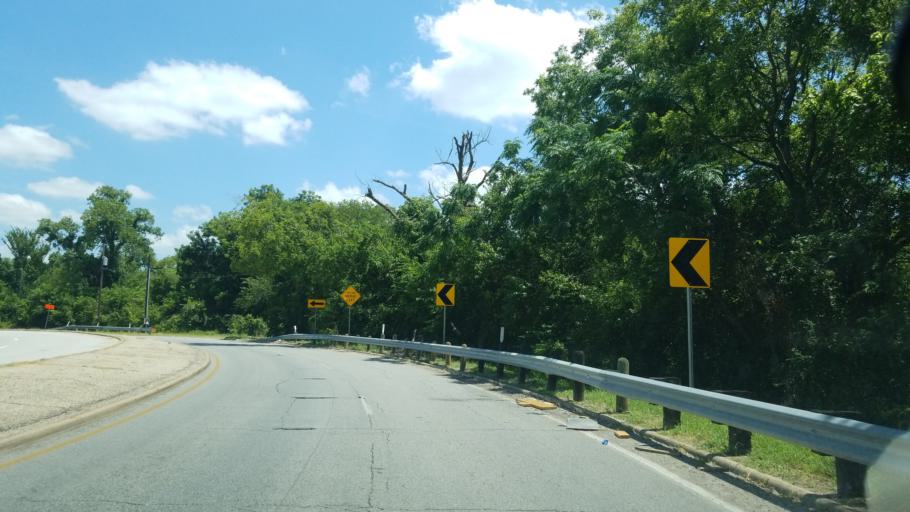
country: US
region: Texas
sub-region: Dallas County
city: Dallas
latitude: 32.7440
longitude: -96.7270
